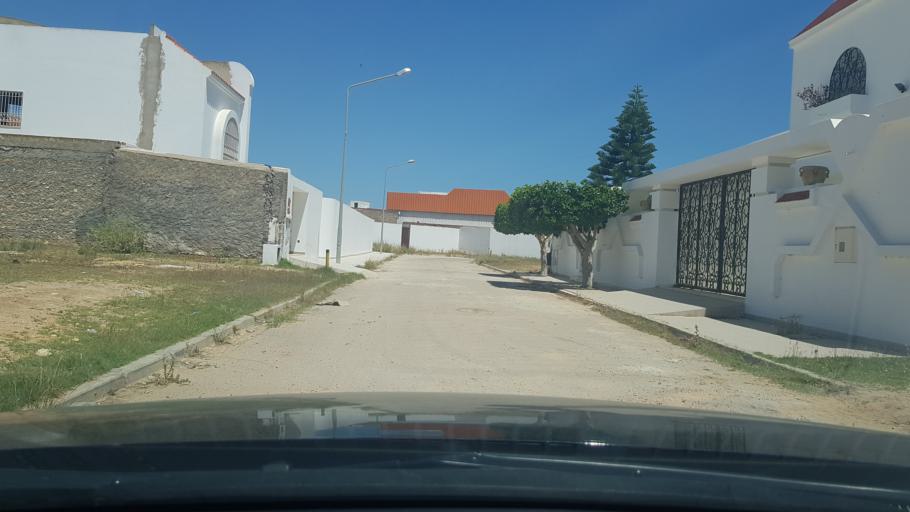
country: TN
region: Safaqis
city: Al Qarmadah
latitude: 34.8372
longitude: 10.7630
